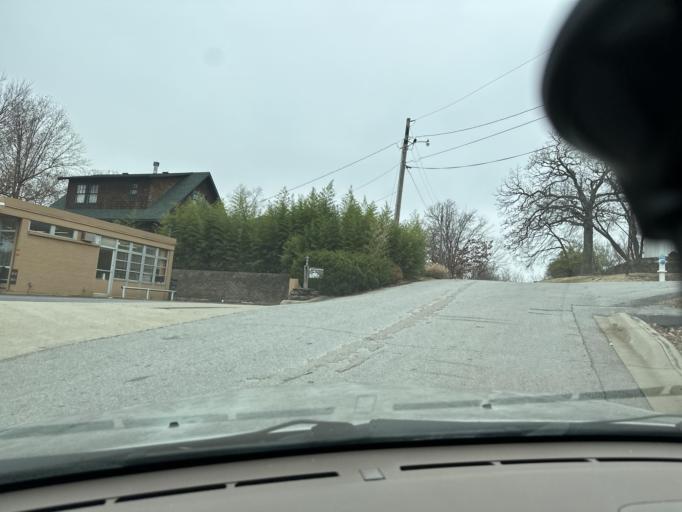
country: US
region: Arkansas
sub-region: Washington County
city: Fayetteville
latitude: 36.0738
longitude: -94.1577
